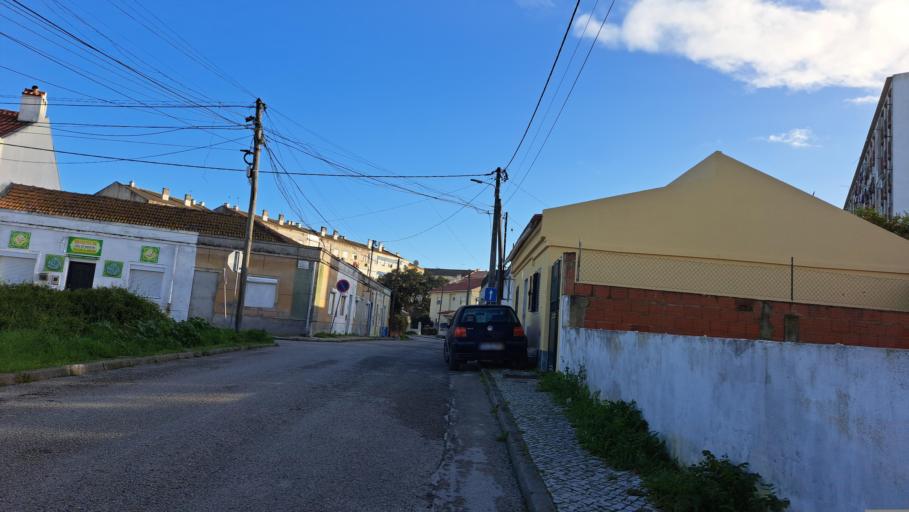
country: PT
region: Setubal
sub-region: Moita
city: Alhos Vedros
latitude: 38.6483
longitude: -9.0388
